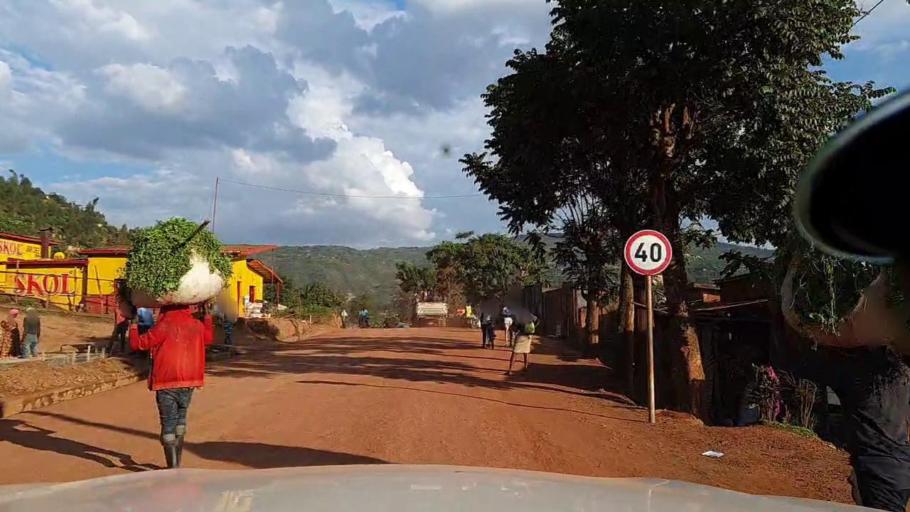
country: RW
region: Kigali
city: Kigali
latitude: -1.9447
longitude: 30.0078
